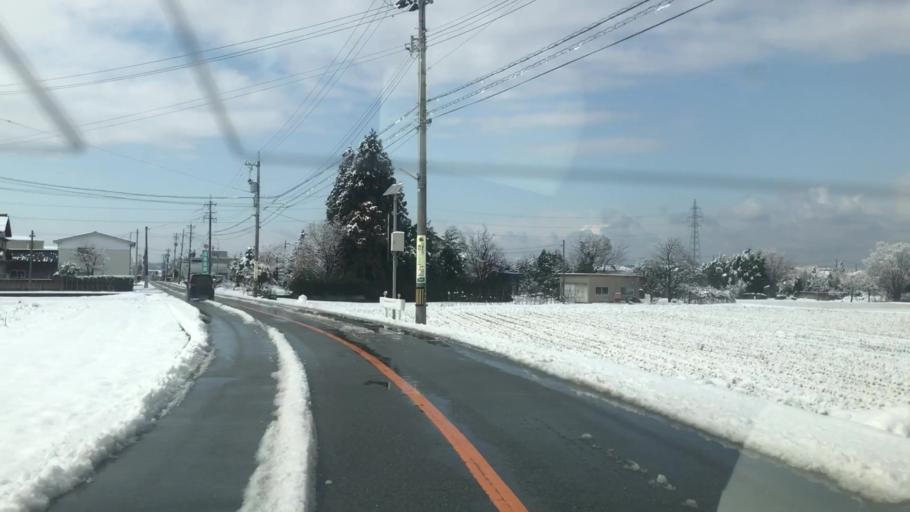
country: JP
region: Toyama
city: Toyama-shi
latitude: 36.6317
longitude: 137.2275
